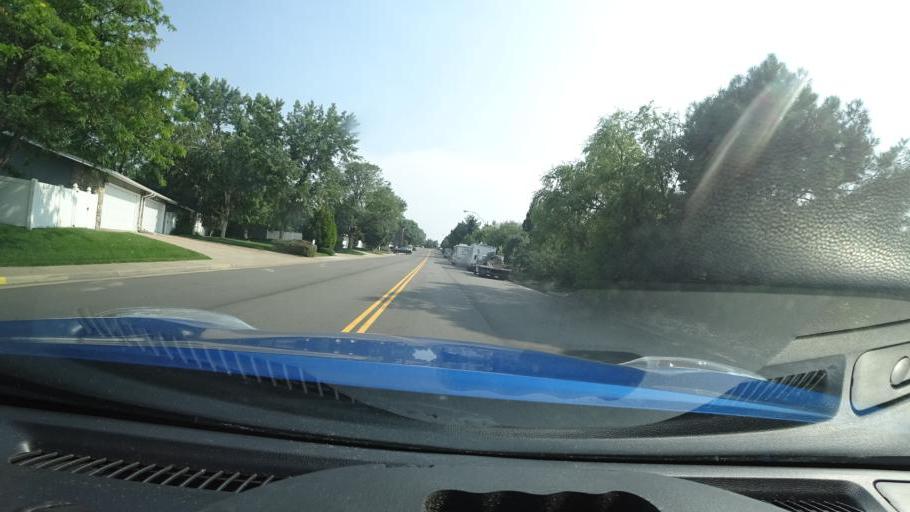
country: US
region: Colorado
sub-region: Adams County
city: Aurora
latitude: 39.6668
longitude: -104.8356
